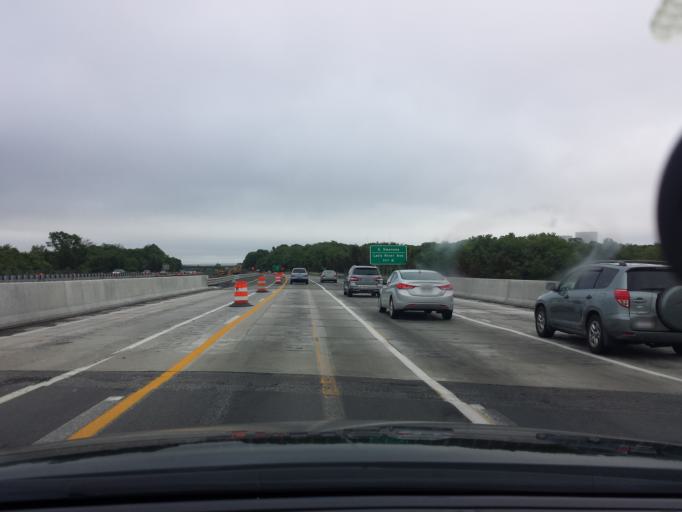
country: US
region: Massachusetts
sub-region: Bristol County
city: Ocean Grove
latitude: 41.7362
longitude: -71.2034
